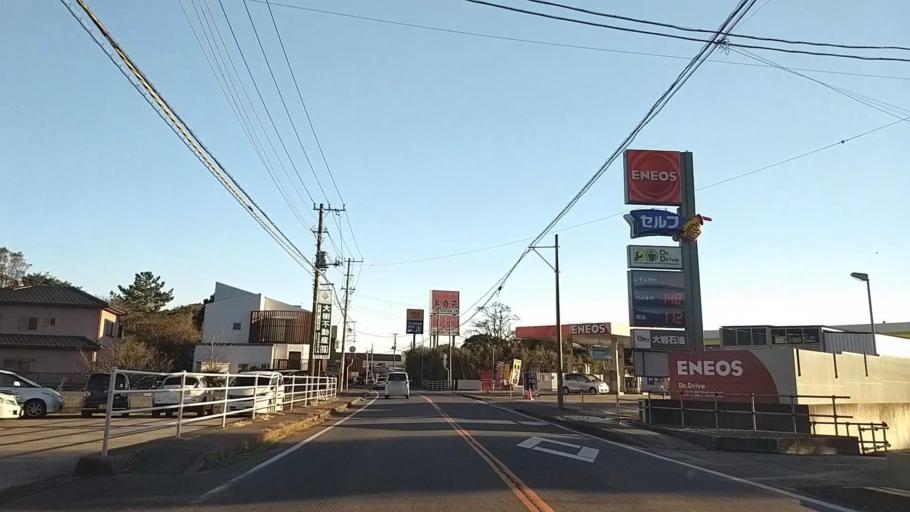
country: JP
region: Chiba
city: Hasaki
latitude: 35.7442
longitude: 140.7910
